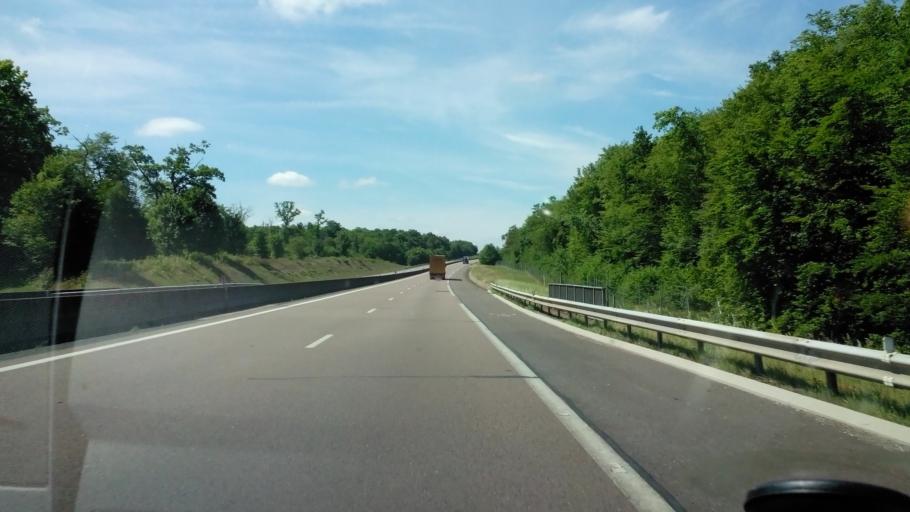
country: FR
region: Lorraine
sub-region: Departement de Meurthe-et-Moselle
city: Colombey-les-Belles
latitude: 48.4846
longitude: 5.8990
